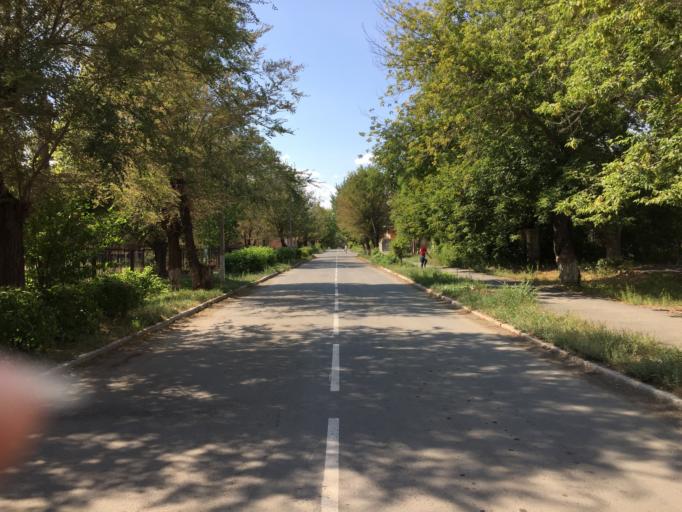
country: RU
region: Orenburg
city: Novotroitsk
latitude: 51.1975
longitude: 58.3284
